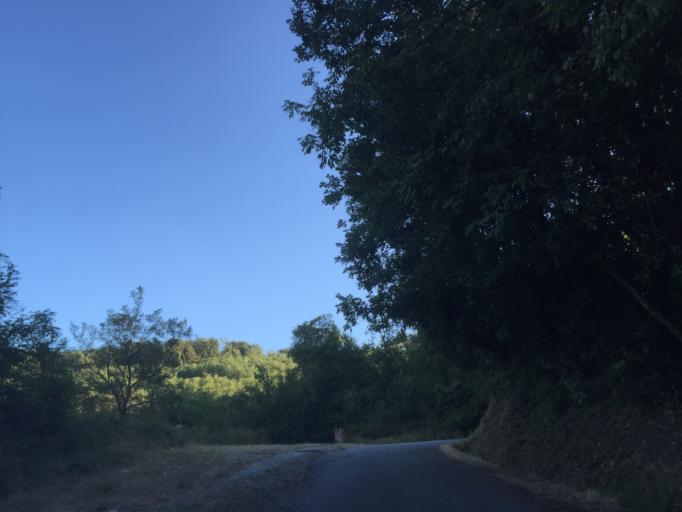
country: IT
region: Tuscany
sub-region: Provincia di Pistoia
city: Pistoia
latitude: 43.9501
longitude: 10.9606
